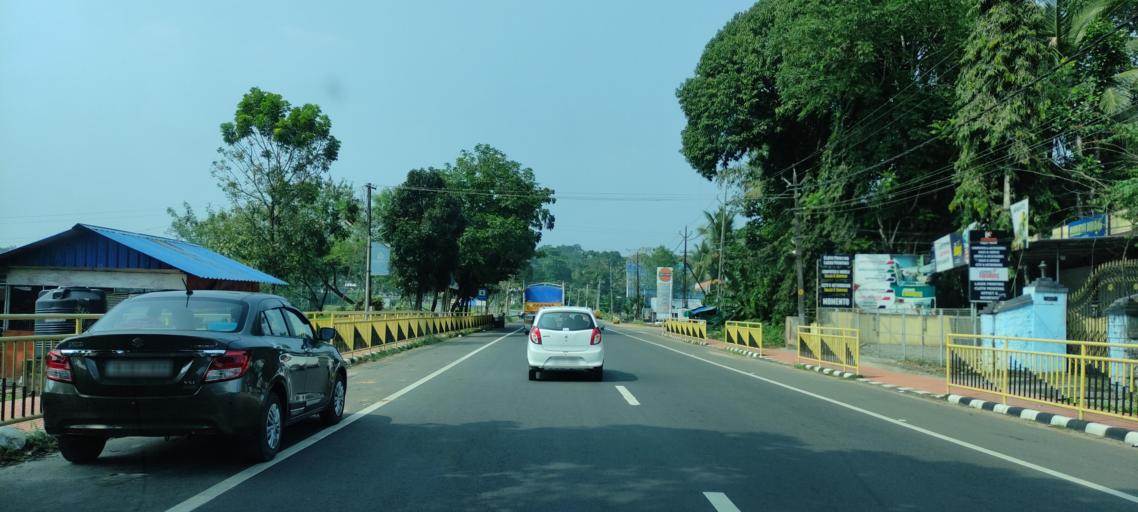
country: IN
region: Kerala
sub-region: Alappuzha
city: Chengannur
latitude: 9.2474
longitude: 76.6686
